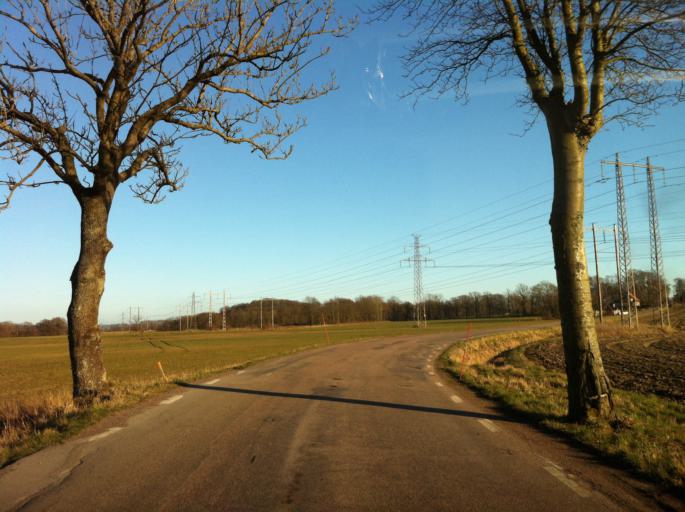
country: SE
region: Skane
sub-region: Helsingborg
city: Morarp
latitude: 56.0744
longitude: 12.8527
